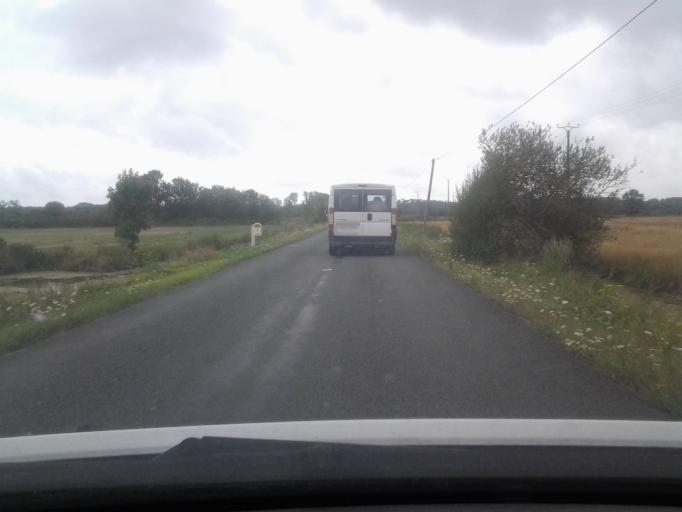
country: FR
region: Pays de la Loire
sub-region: Departement de la Vendee
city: La Tranche-sur-Mer
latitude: 46.3878
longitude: -1.4551
